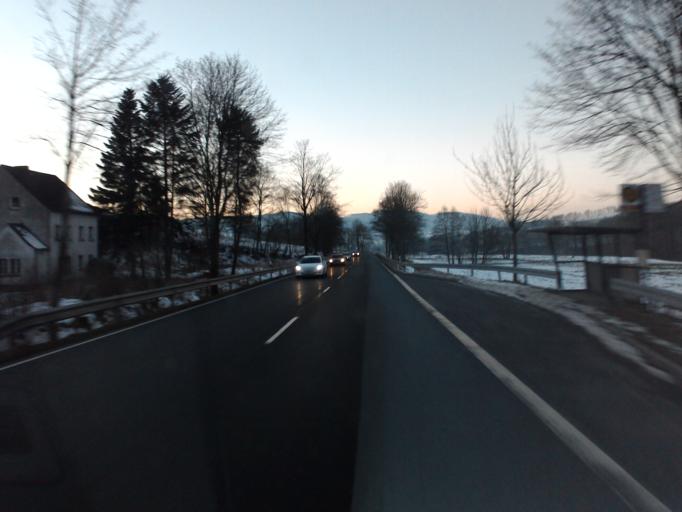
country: DE
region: North Rhine-Westphalia
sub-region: Regierungsbezirk Arnsberg
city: Olsberg
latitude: 51.2811
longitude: 8.5132
